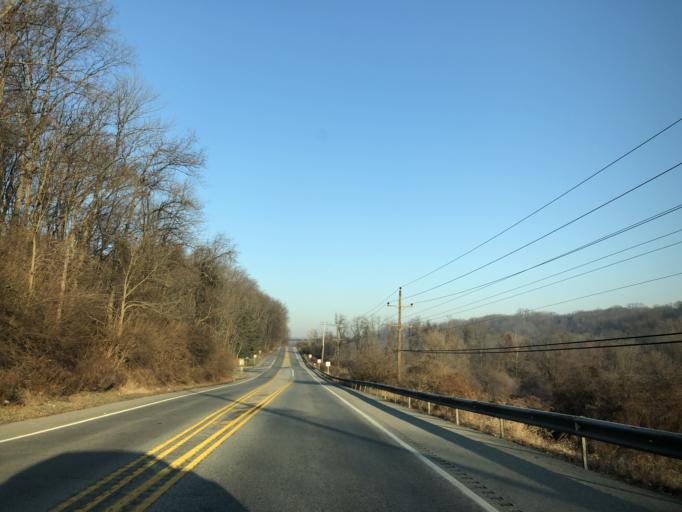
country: US
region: Pennsylvania
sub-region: Chester County
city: Downingtown
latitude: 39.9879
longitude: -75.6923
